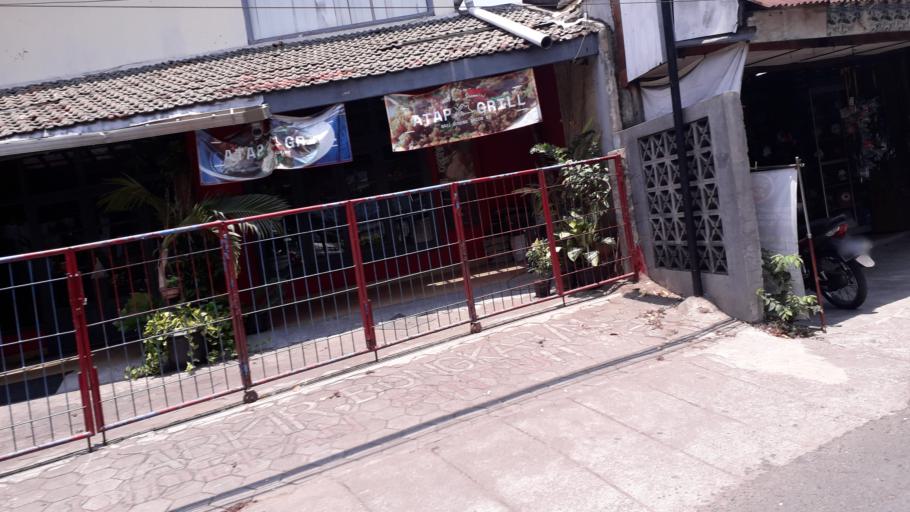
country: ID
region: Daerah Istimewa Yogyakarta
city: Yogyakarta
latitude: -7.7880
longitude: 110.3581
